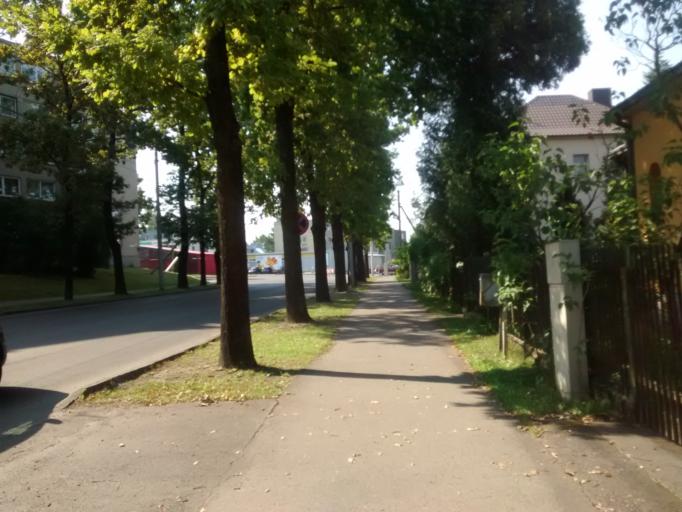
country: LT
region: Kauno apskritis
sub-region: Kaunas
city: Eiguliai
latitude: 54.9153
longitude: 23.9206
